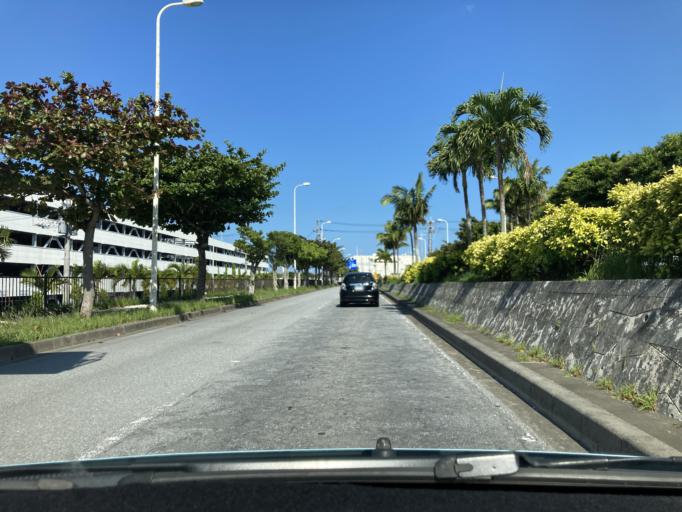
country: JP
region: Okinawa
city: Naha-shi
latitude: 26.2098
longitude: 127.6522
